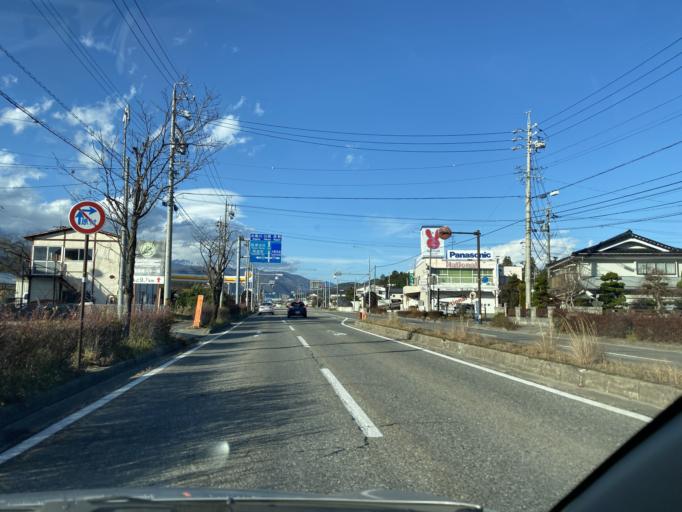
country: JP
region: Nagano
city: Omachi
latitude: 36.5122
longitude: 137.8526
